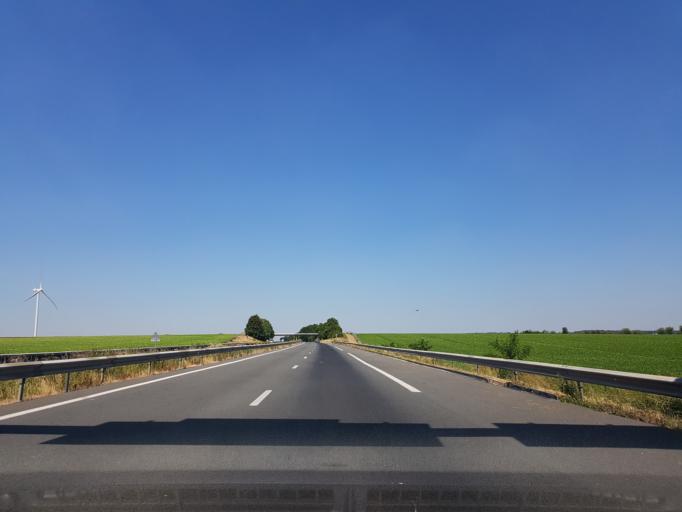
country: FR
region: Nord-Pas-de-Calais
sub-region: Departement du Nord
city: Marcoing
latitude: 50.1329
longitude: 3.1450
